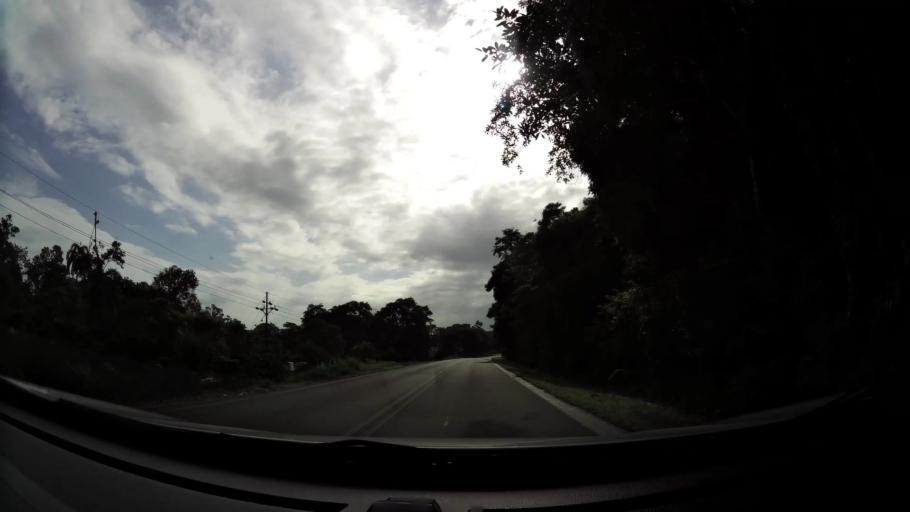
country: CR
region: Limon
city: Pocora
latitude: 10.1942
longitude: -83.6433
